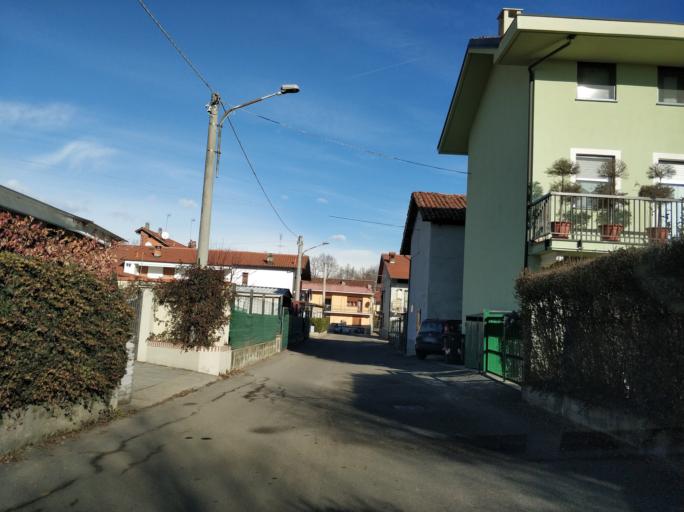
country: IT
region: Piedmont
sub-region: Provincia di Torino
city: San Carlo Canavese
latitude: 45.2508
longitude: 7.6016
